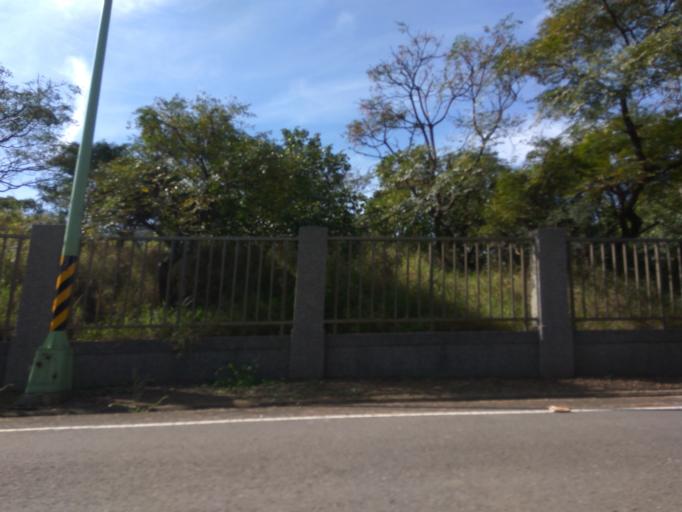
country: TW
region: Taiwan
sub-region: Hsinchu
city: Zhubei
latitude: 25.0333
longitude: 121.0532
